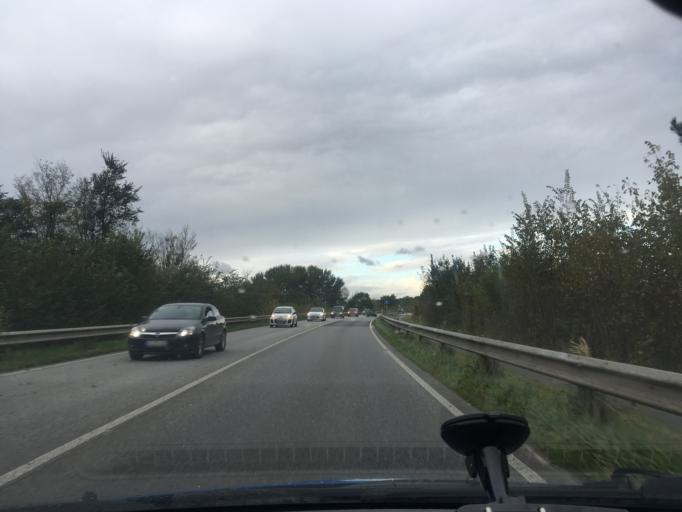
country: DE
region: Lower Saxony
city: Marschacht
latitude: 53.4284
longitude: 10.3352
